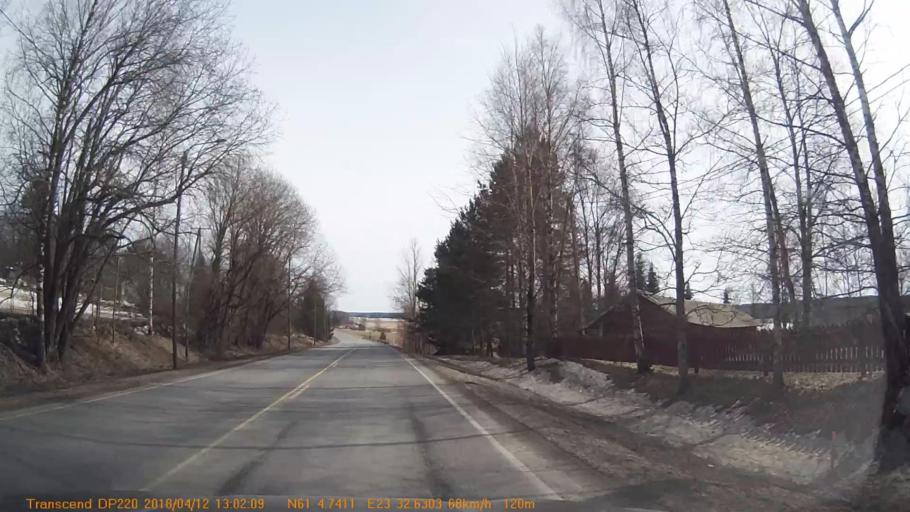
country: FI
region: Pirkanmaa
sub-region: Etelae-Pirkanmaa
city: Urjala
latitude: 61.0789
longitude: 23.5445
